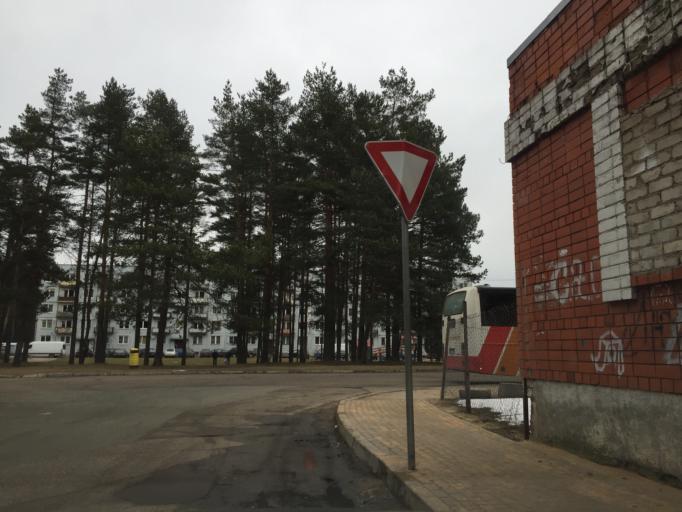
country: LV
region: Garkalne
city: Garkalne
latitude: 56.9636
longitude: 24.4293
